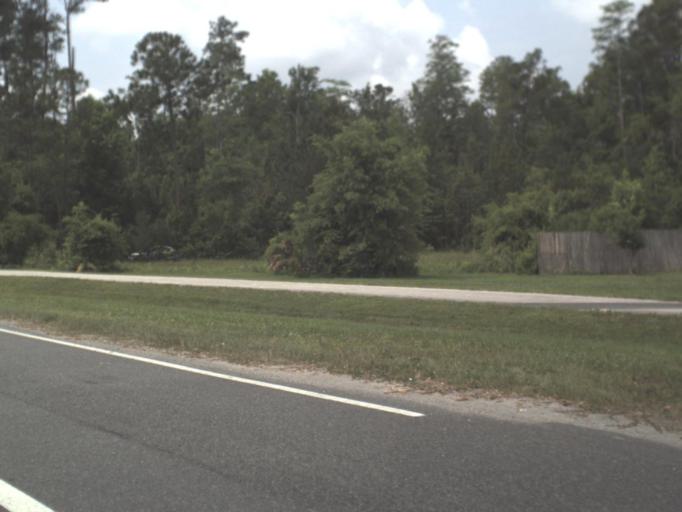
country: US
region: Florida
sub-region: Clay County
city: Green Cove Springs
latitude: 30.0594
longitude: -81.7079
